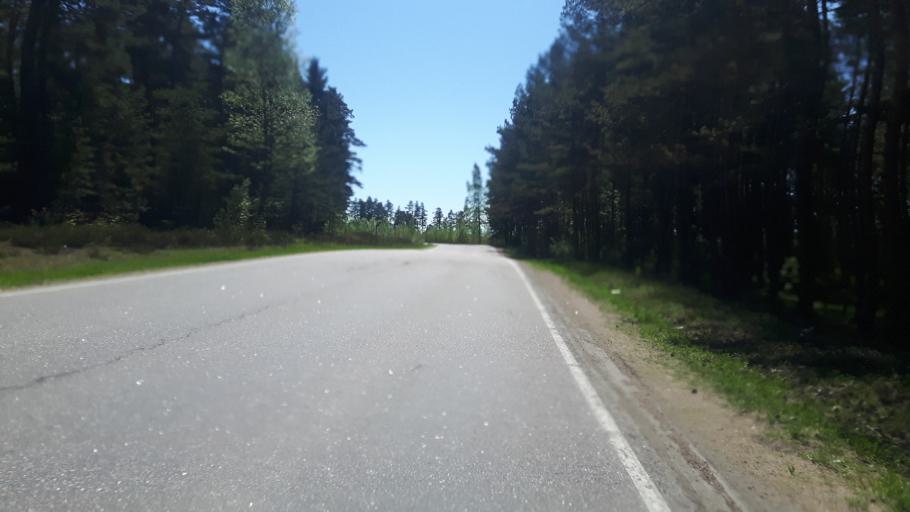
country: RU
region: Leningrad
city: Glebychevo
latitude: 60.3348
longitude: 28.8208
